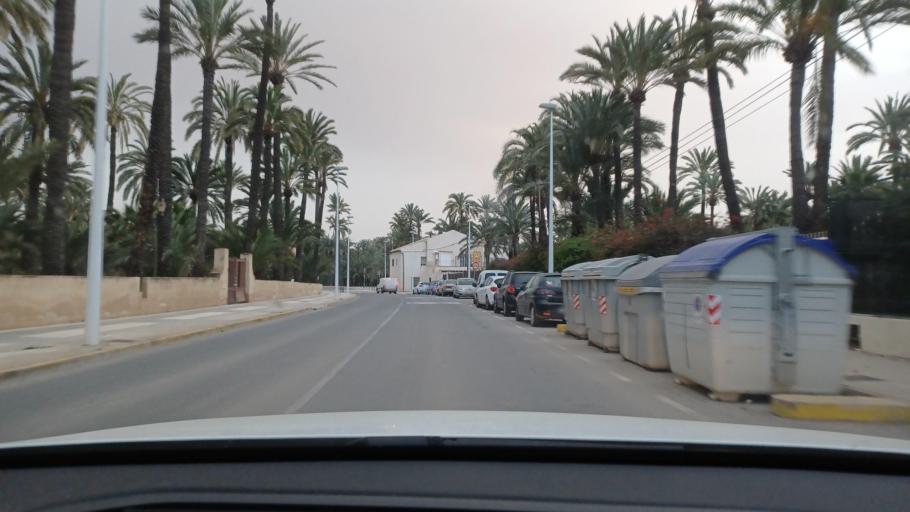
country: ES
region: Valencia
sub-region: Provincia de Alicante
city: Elche
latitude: 38.2594
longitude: -0.6932
